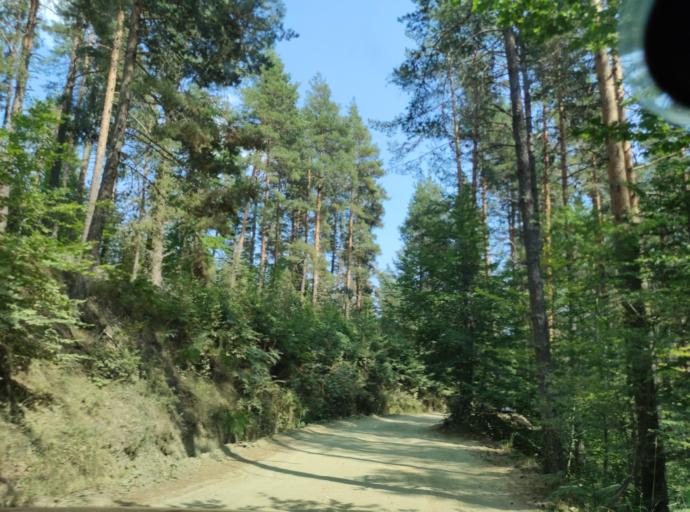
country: BG
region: Blagoevgrad
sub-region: Obshtina Belitsa
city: Belitsa
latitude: 42.0249
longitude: 23.5810
